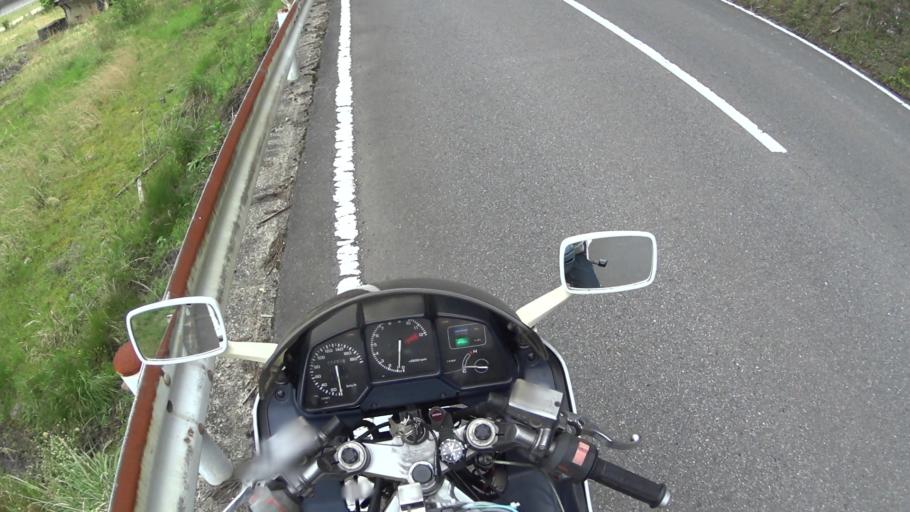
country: JP
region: Kyoto
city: Kameoka
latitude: 35.1394
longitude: 135.6096
